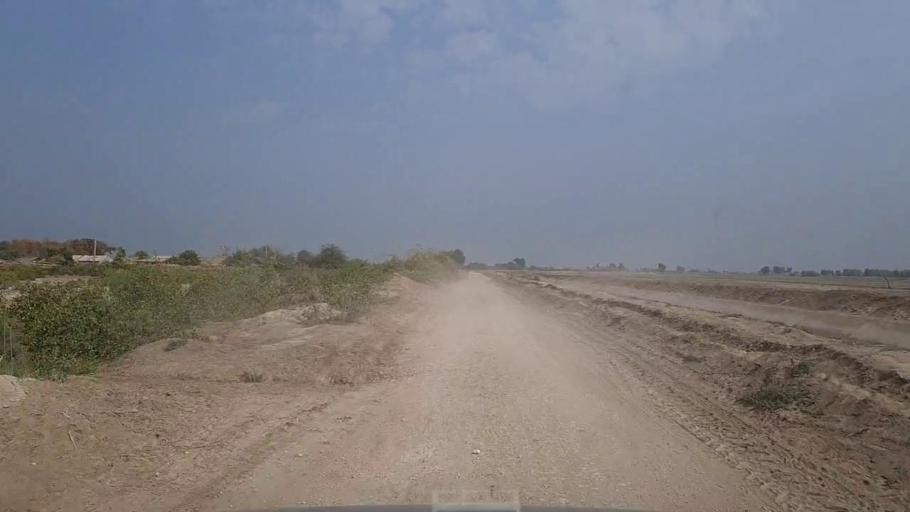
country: PK
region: Sindh
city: Mirwah Gorchani
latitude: 25.3993
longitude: 69.0772
